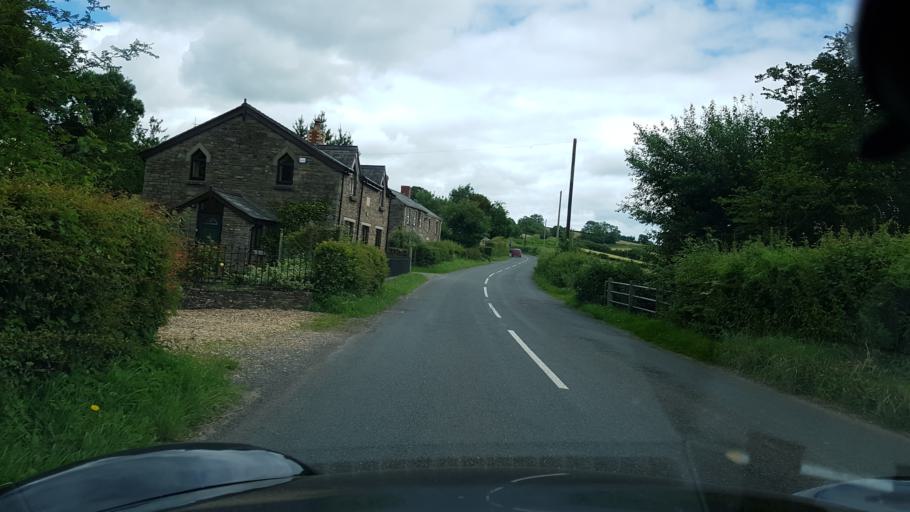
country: GB
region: Wales
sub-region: Monmouthshire
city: Grosmont
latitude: 51.8581
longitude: -2.8989
